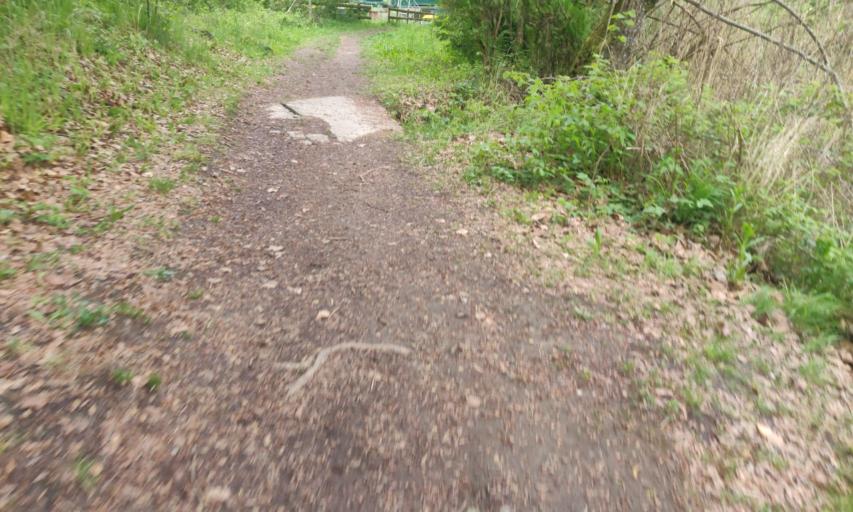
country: CH
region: Fribourg
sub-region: Sarine District
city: Marly
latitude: 46.7860
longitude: 7.1580
